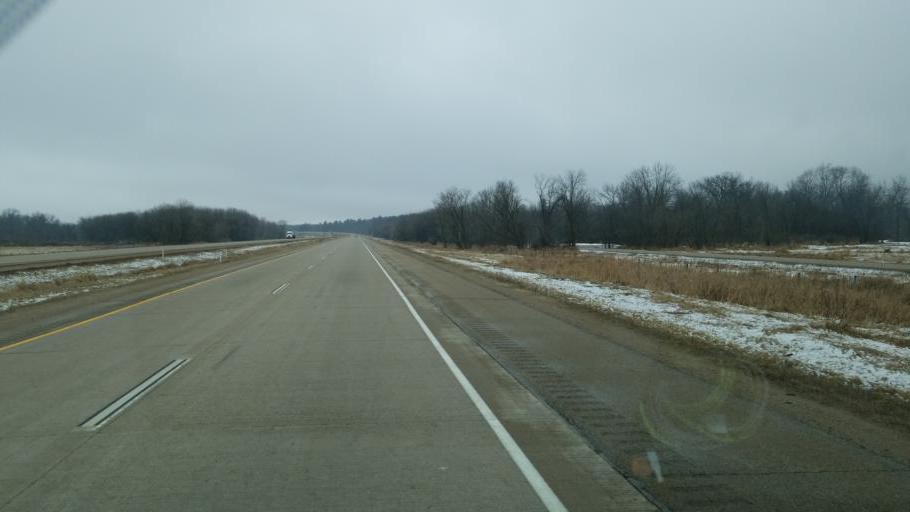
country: US
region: Wisconsin
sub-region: Waupaca County
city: Weyauwega
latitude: 44.2458
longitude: -88.8035
